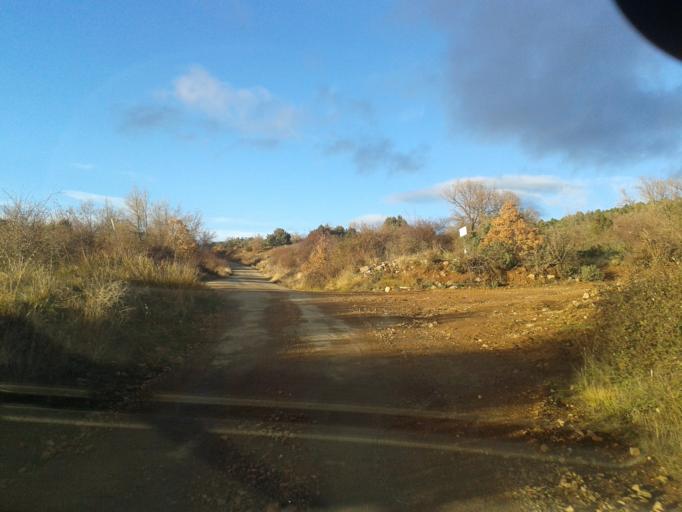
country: ES
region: Aragon
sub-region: Provincia de Teruel
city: Lagueruela
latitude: 41.0136
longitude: -1.1798
